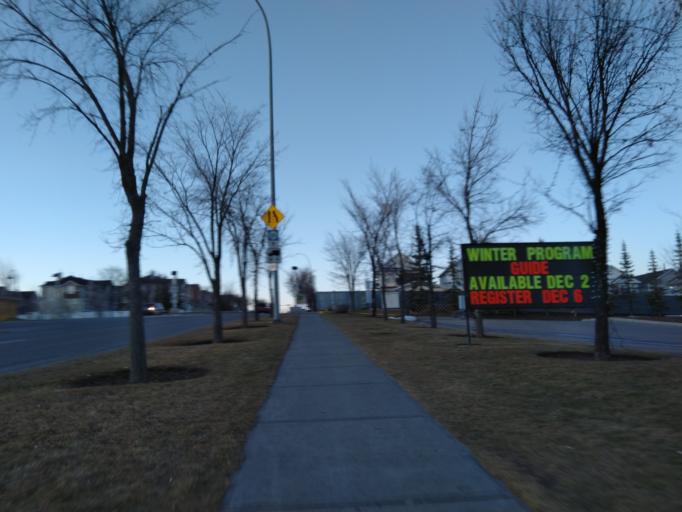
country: CA
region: Alberta
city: Calgary
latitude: 51.1246
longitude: -114.2463
